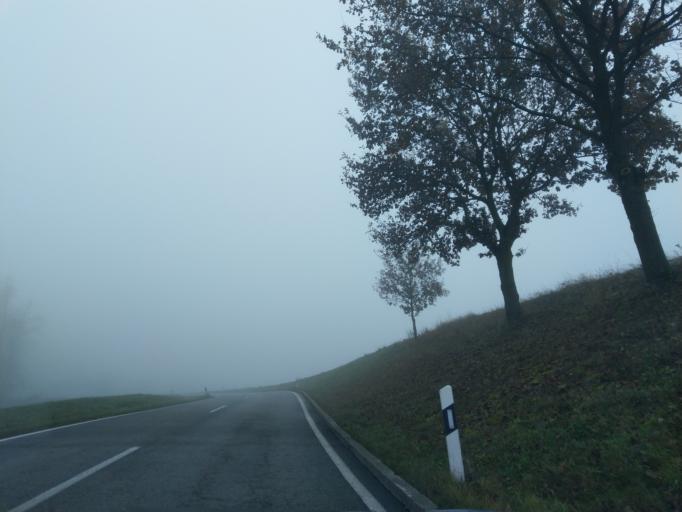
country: DE
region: Bavaria
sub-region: Lower Bavaria
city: Auerbach
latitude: 48.7753
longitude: 13.0963
